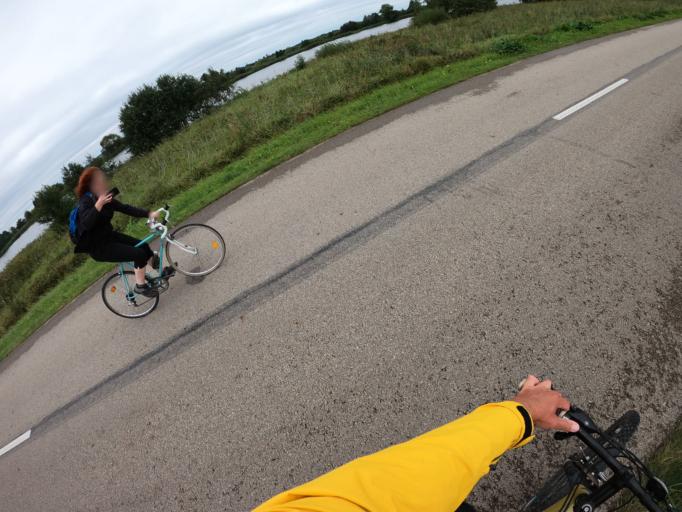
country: LT
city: Rusne
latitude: 55.3432
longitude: 21.3384
